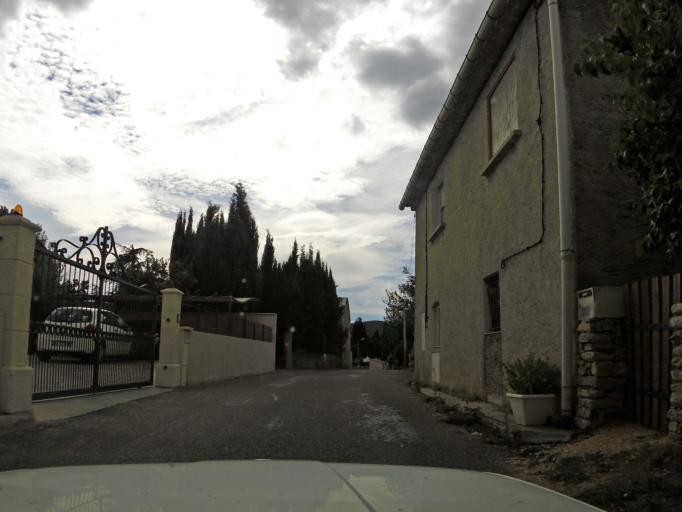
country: FR
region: Languedoc-Roussillon
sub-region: Departement du Gard
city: Saint-Christol-les-Ales
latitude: 44.0855
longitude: 4.0713
